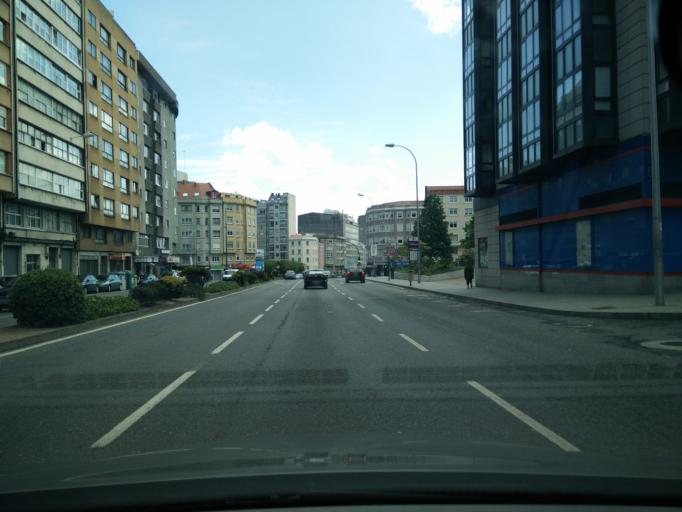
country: ES
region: Galicia
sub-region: Provincia da Coruna
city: A Coruna
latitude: 43.3561
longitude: -8.4151
